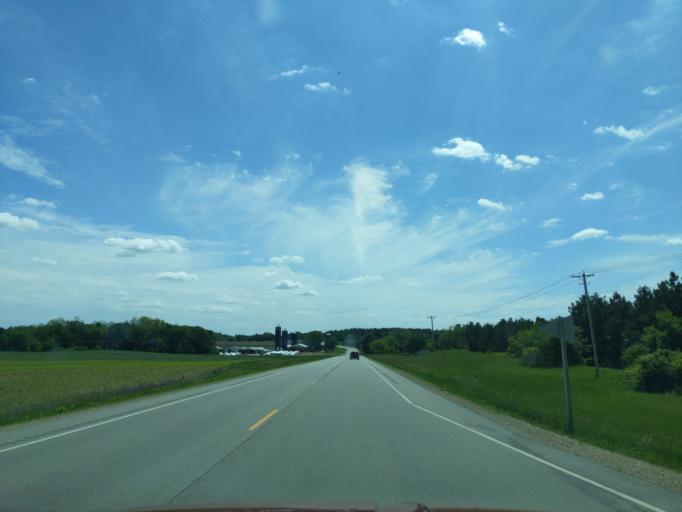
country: US
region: Wisconsin
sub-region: Columbia County
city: Pardeeville
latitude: 43.4662
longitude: -89.3189
